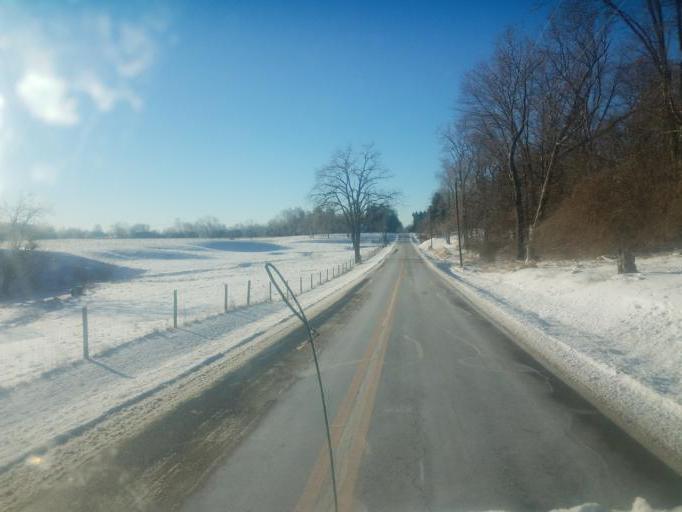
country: US
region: Ohio
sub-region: Delaware County
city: Sunbury
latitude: 40.2276
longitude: -82.9120
